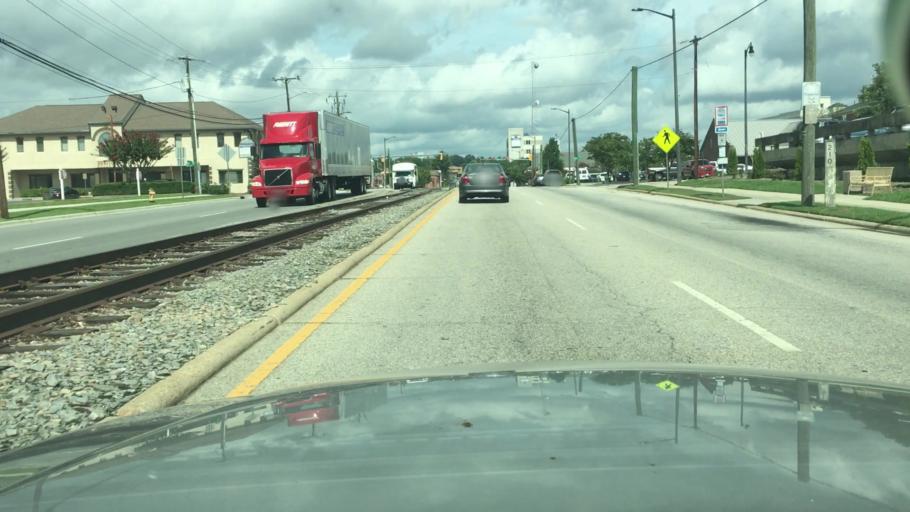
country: US
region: North Carolina
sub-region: Cumberland County
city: Fayetteville
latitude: 35.0499
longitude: -78.8770
